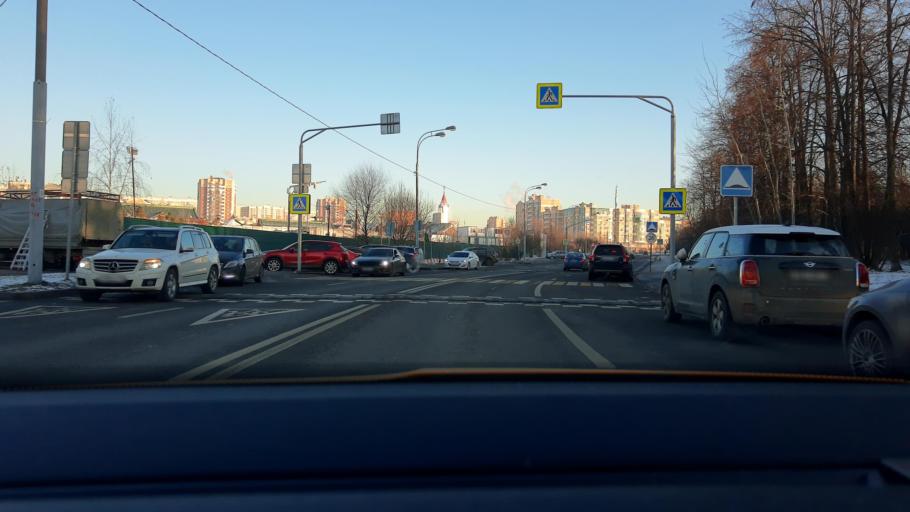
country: RU
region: Moscow
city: Khimki
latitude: 55.8995
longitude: 37.3828
